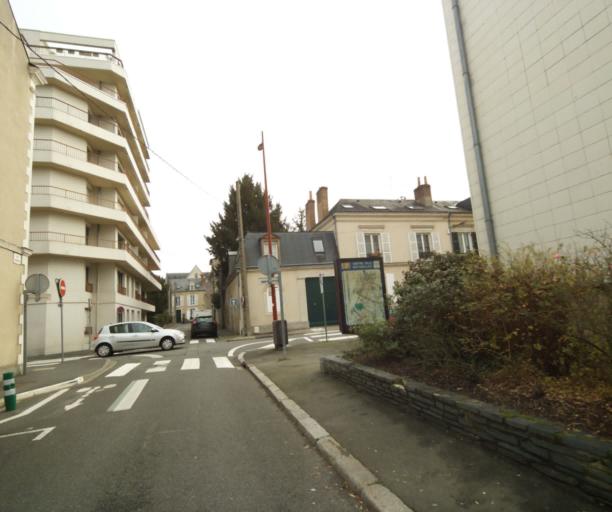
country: FR
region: Pays de la Loire
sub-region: Departement de la Sarthe
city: Le Mans
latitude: 48.0036
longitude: 0.2071
